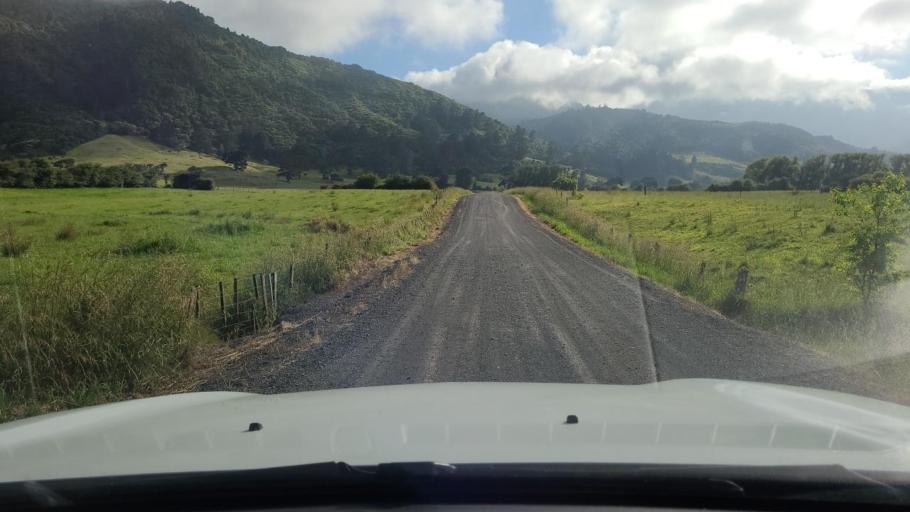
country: NZ
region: Bay of Plenty
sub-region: Western Bay of Plenty District
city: Katikati
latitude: -37.5648
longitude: 175.7399
